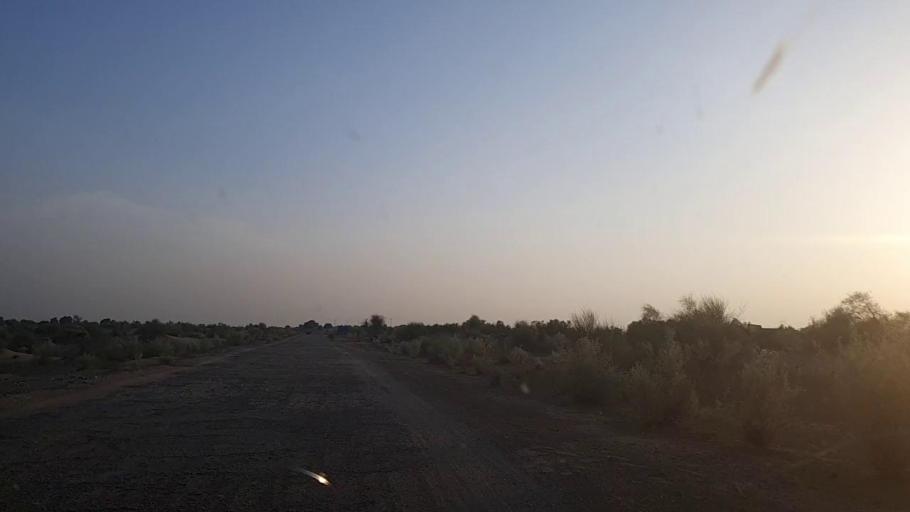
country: PK
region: Sindh
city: Khanpur
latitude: 27.6018
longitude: 69.4313
